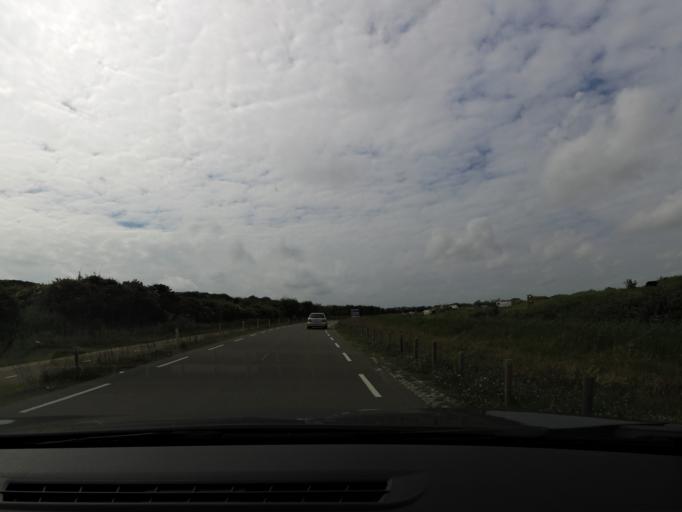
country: NL
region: Zeeland
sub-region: Gemeente Vlissingen
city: Vlissingen
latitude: 51.5071
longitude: 3.4699
